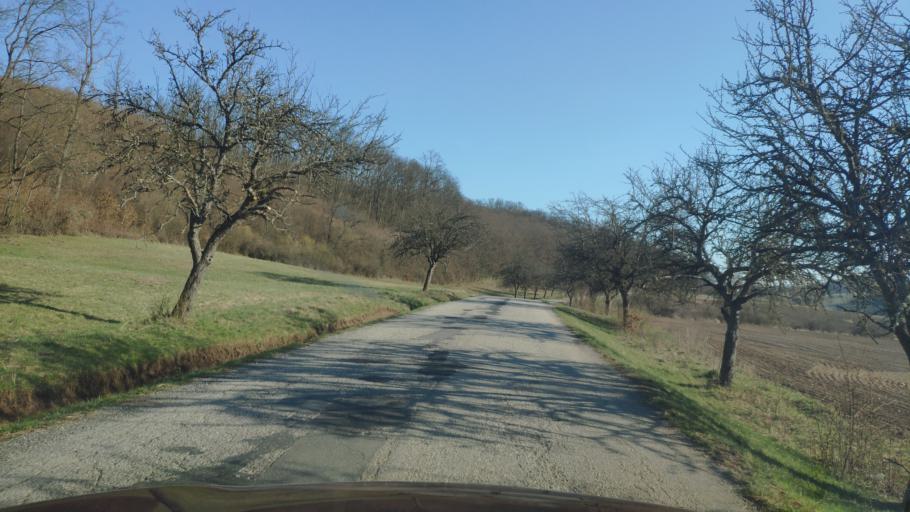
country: SK
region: Banskobystricky
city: Revuca
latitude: 48.5276
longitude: 20.2517
